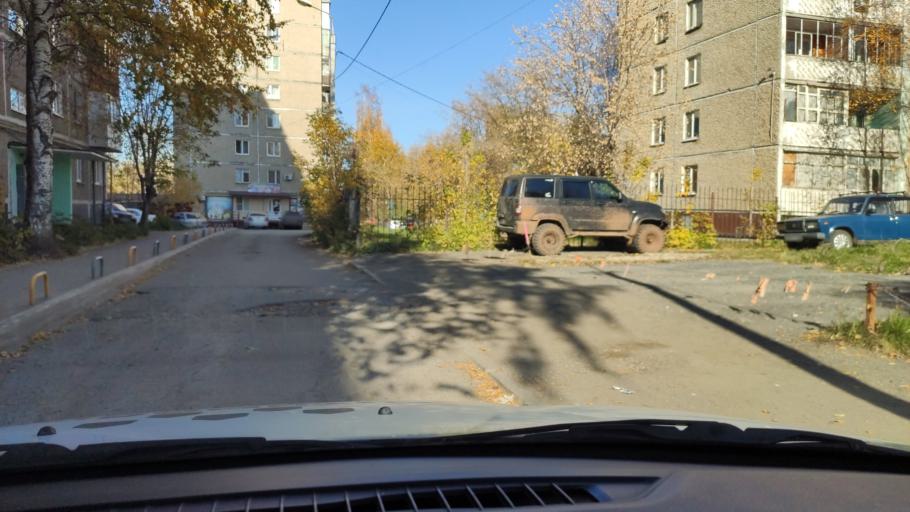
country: RU
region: Perm
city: Perm
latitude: 57.9657
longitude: 56.2128
